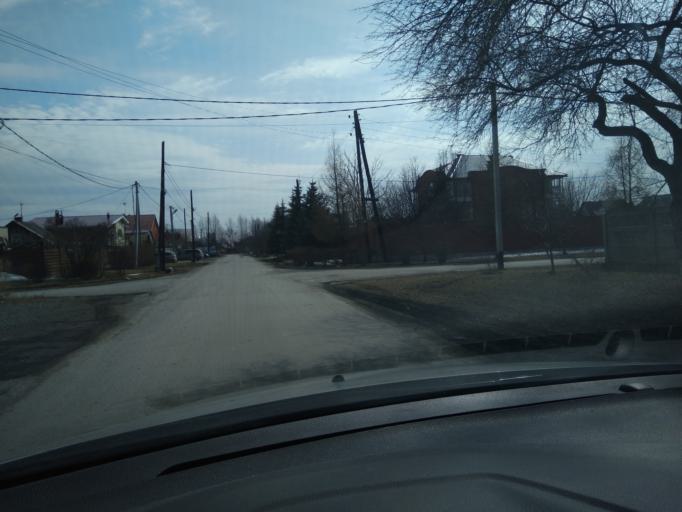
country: RU
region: Sverdlovsk
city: Shuvakish
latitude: 56.8891
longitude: 60.4855
